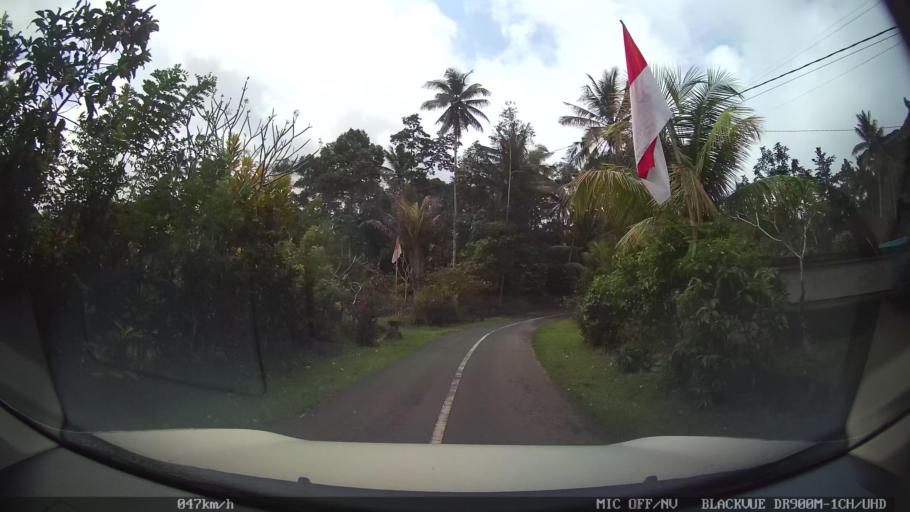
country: ID
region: Bali
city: Pegongan
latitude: -8.4722
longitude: 115.2333
